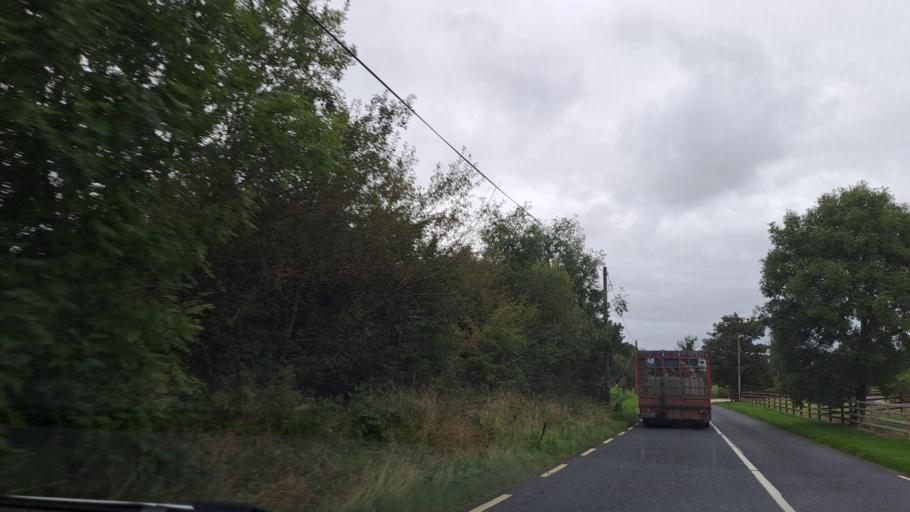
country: IE
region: Ulster
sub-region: County Monaghan
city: Castleblayney
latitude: 54.0934
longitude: -6.8442
